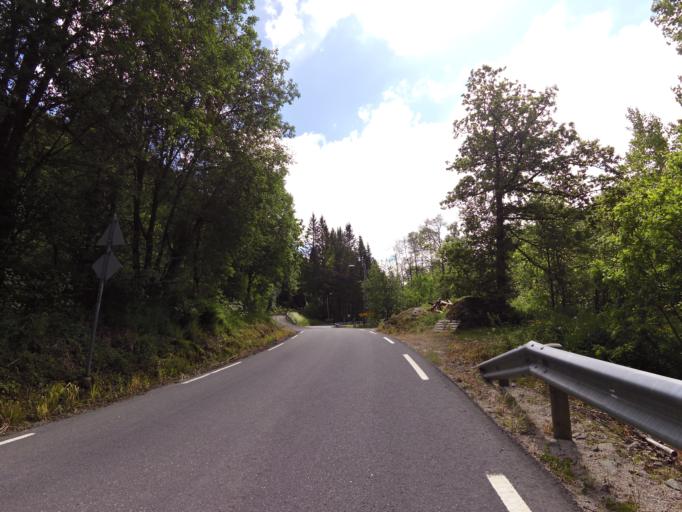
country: NO
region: Vest-Agder
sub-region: Kvinesdal
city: Liknes
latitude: 58.2880
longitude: 6.9391
